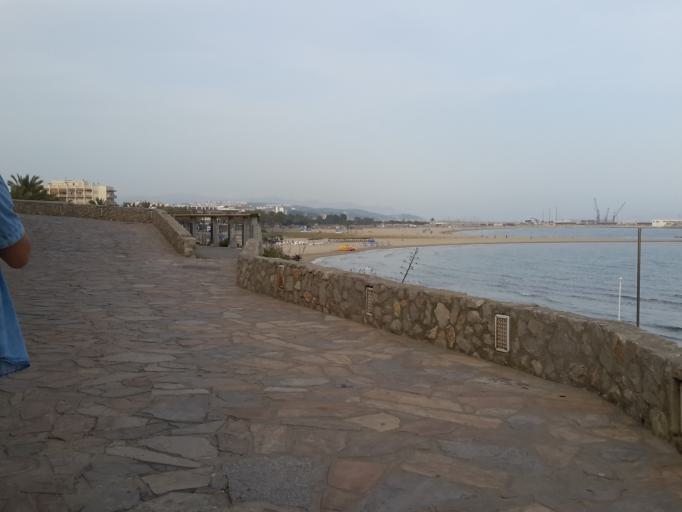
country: ES
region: Catalonia
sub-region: Provincia de Barcelona
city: Vilanova i la Geltru
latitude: 41.2106
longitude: 1.7130
